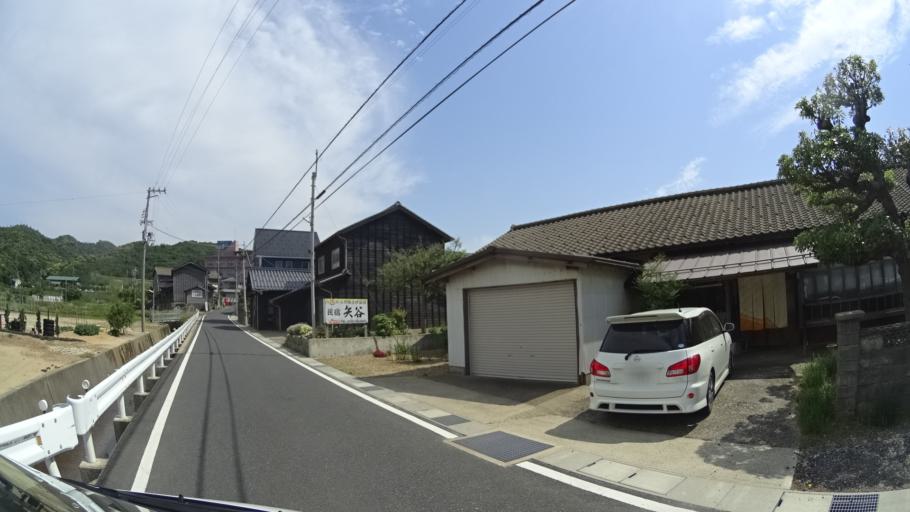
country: JP
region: Kyoto
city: Miyazu
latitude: 35.6993
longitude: 135.0542
